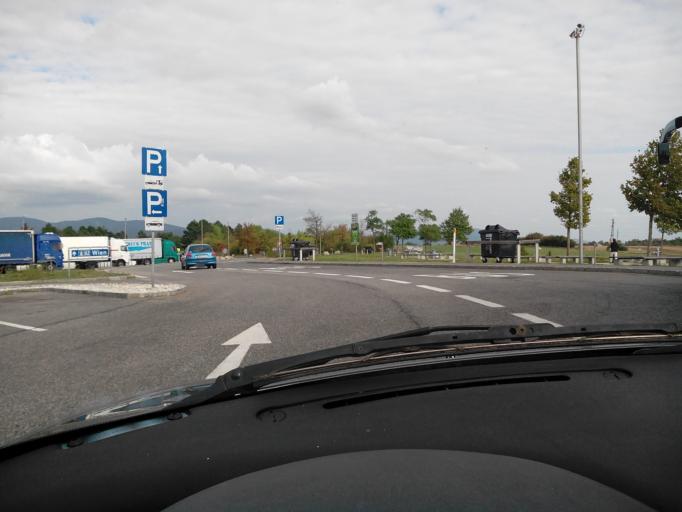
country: AT
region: Lower Austria
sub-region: Politischer Bezirk Baden
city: Leobersdorf
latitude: 47.9089
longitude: 16.2089
